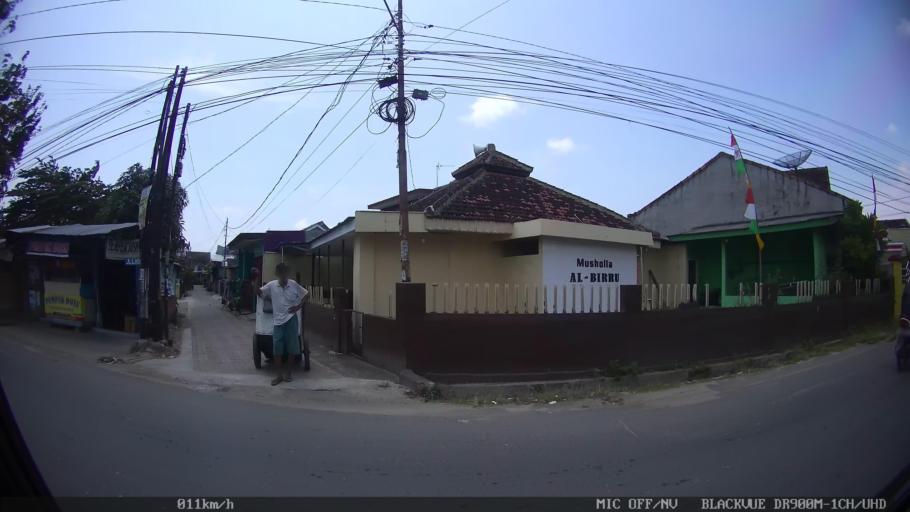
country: ID
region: Lampung
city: Kedaton
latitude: -5.3752
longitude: 105.2734
